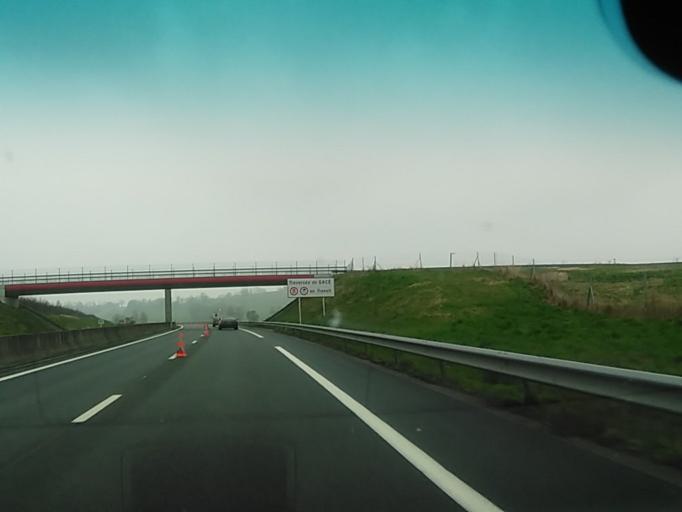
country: FR
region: Lower Normandy
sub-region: Departement de l'Orne
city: Gace
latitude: 48.7226
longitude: 0.2611
